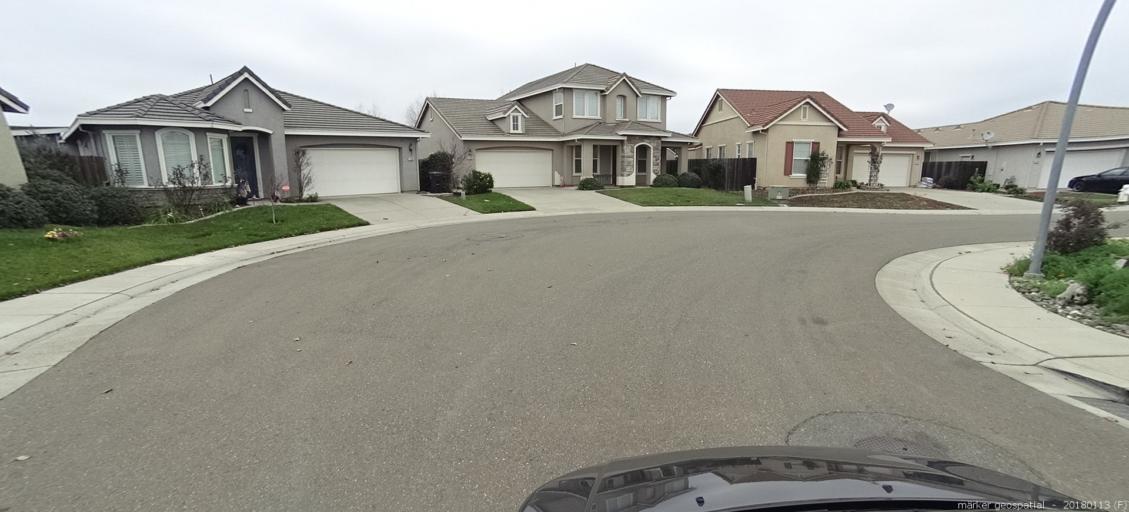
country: US
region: California
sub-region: Sacramento County
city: Gold River
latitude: 38.5523
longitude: -121.2153
